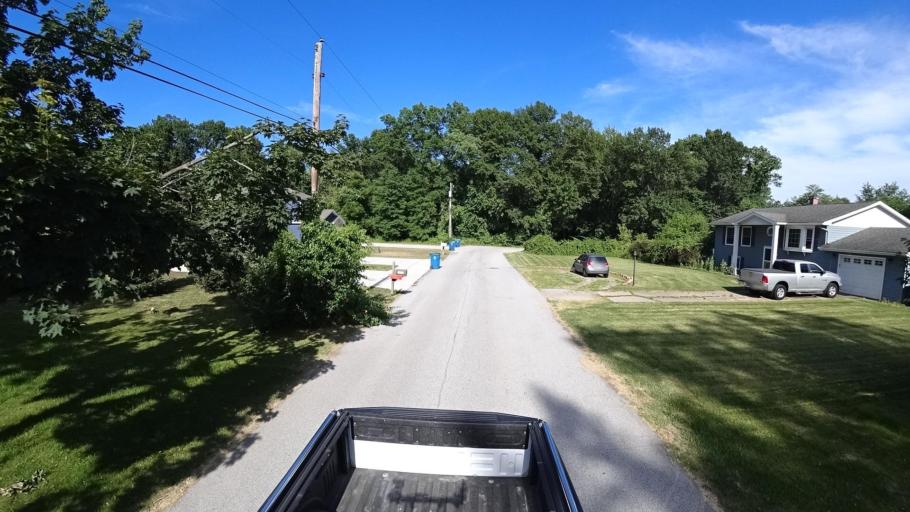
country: US
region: Indiana
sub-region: Porter County
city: Porter
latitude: 41.6145
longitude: -87.0923
